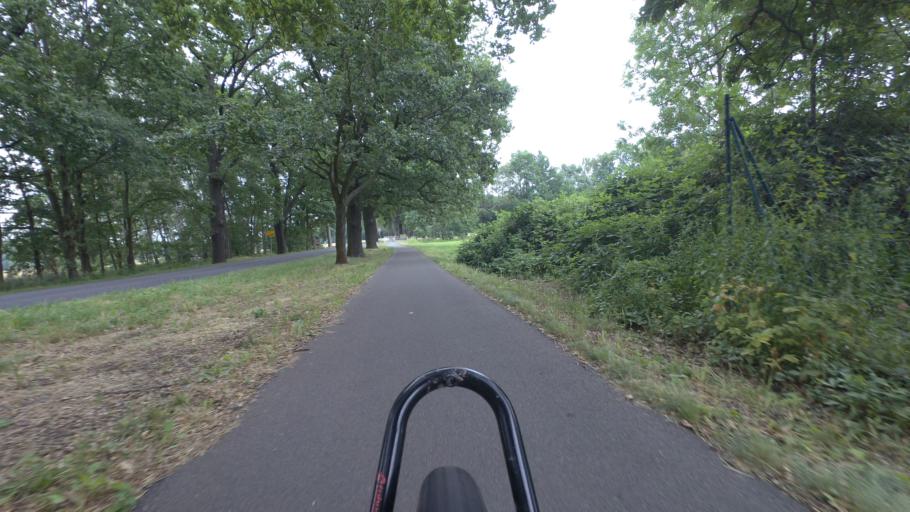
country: DE
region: Brandenburg
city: Luckenwalde
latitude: 52.0891
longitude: 13.1946
